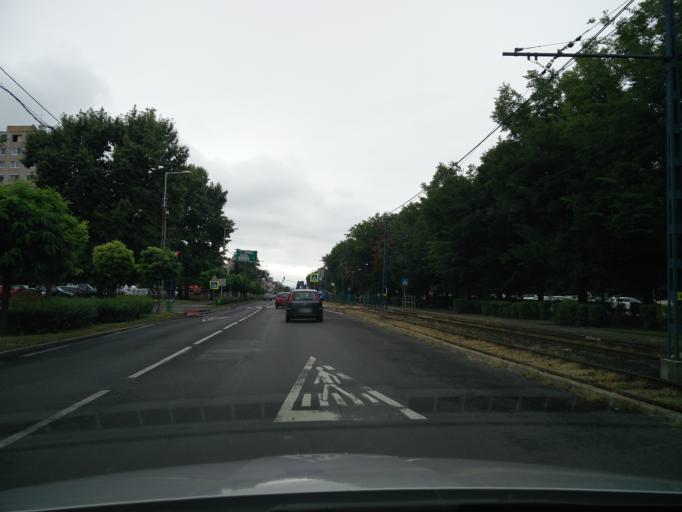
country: HU
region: Budapest
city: Budapest XIX. keruelet
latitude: 47.4560
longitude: 19.1483
